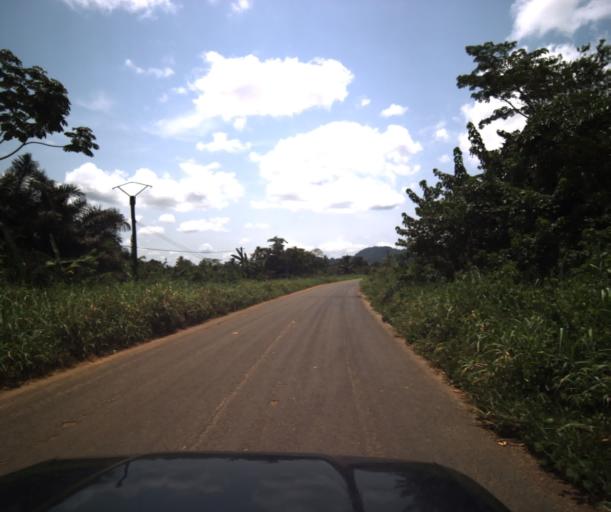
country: CM
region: Centre
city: Eseka
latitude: 3.6518
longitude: 10.7868
